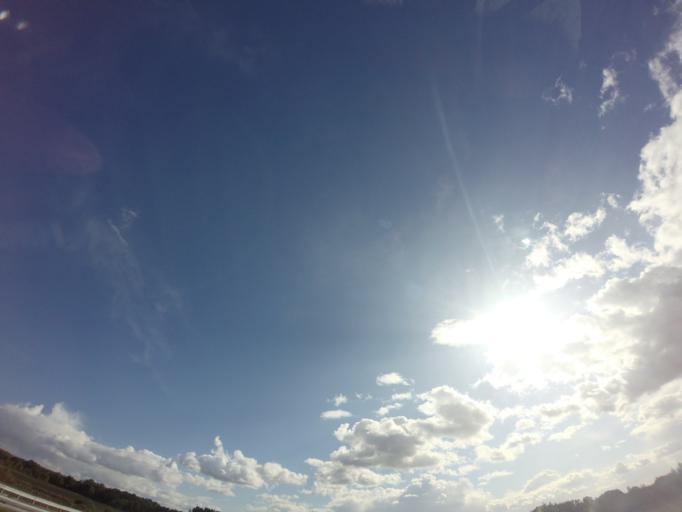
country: PL
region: Lubusz
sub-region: Powiat nowosolski
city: Nowe Miasteczko
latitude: 51.6945
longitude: 15.7538
